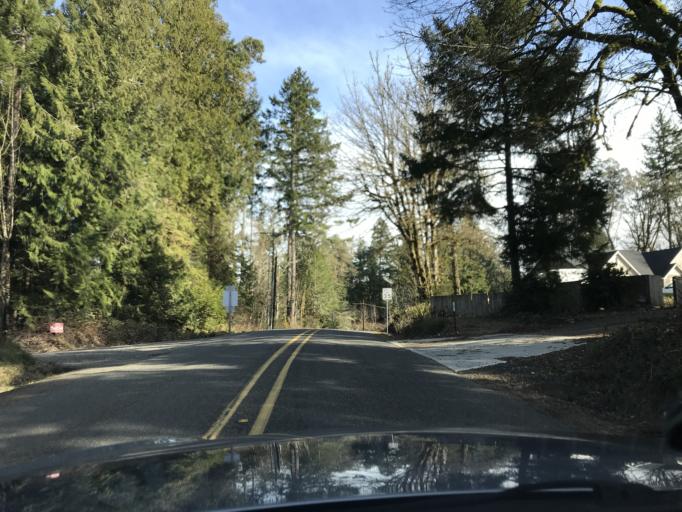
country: US
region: Washington
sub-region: Pierce County
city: Home
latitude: 47.2584
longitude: -122.7644
